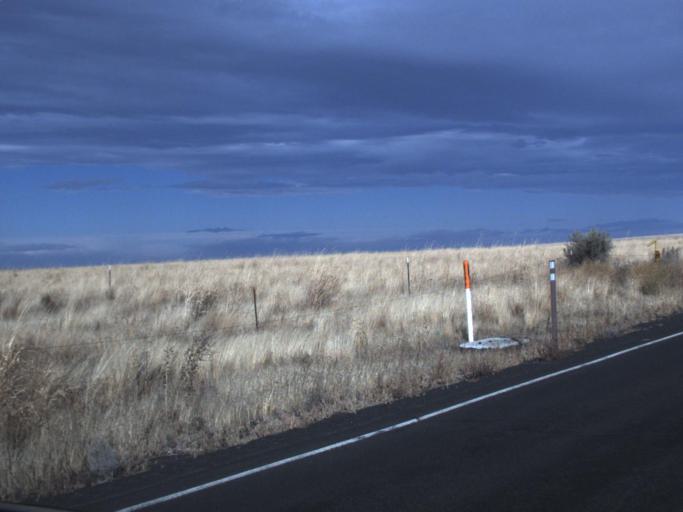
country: US
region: Washington
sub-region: Adams County
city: Ritzville
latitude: 47.3163
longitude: -118.6904
